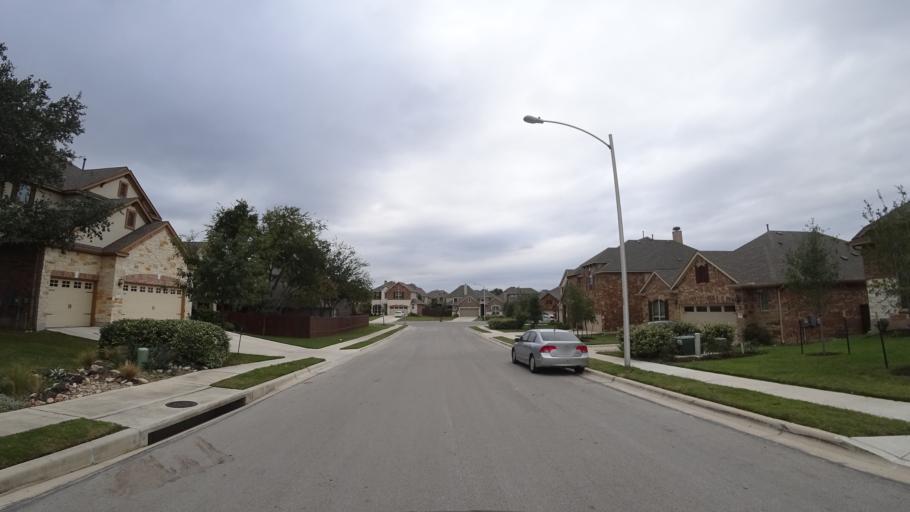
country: US
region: Texas
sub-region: Travis County
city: Manchaca
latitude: 30.1425
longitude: -97.8505
